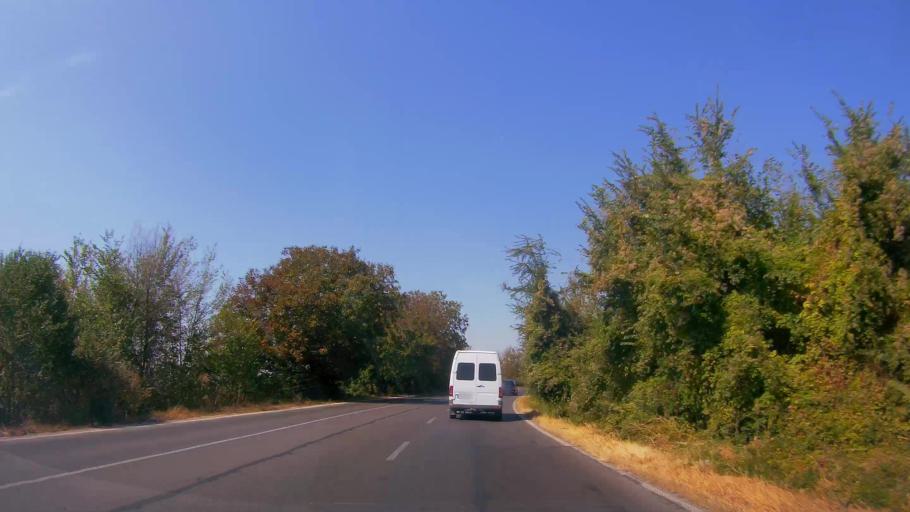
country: BG
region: Razgrad
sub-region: Obshtina Tsar Kaloyan
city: Tsar Kaloyan
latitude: 43.6309
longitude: 26.2029
